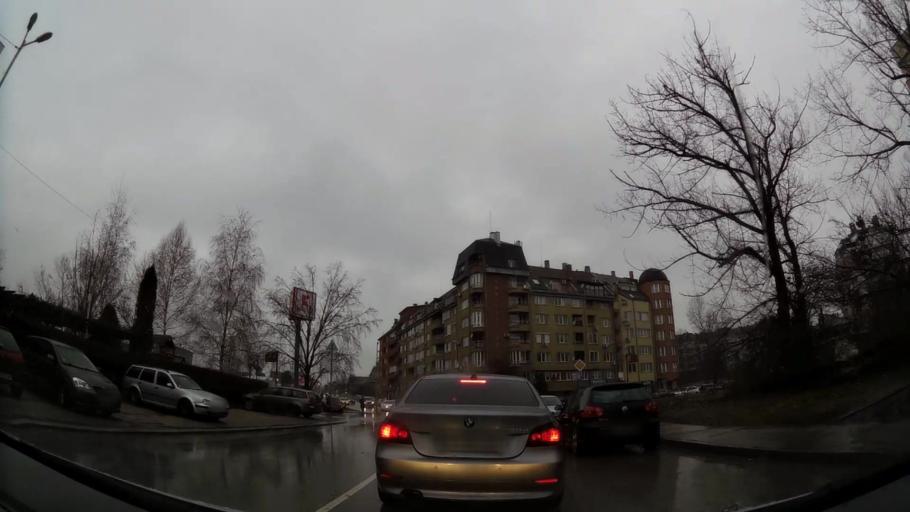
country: BG
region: Sofia-Capital
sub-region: Stolichna Obshtina
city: Sofia
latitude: 42.6432
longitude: 23.3381
